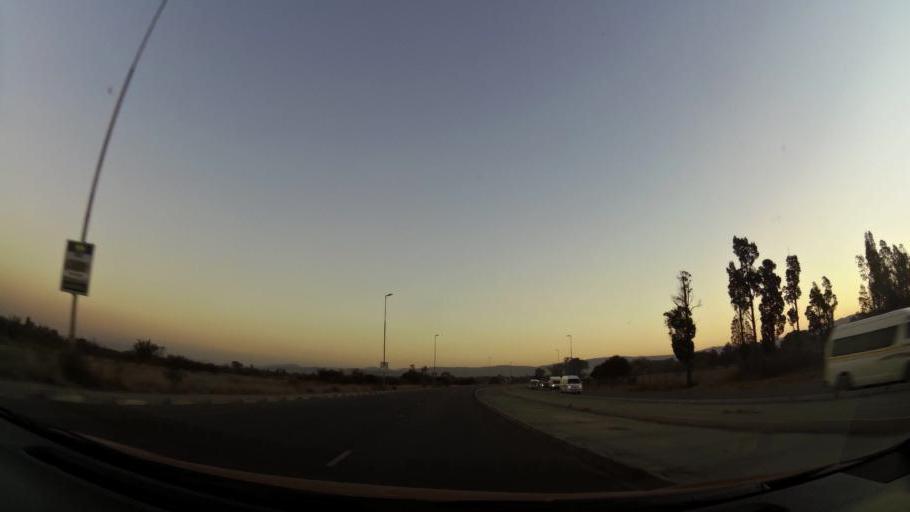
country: ZA
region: North-West
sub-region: Bojanala Platinum District Municipality
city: Rustenburg
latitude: -25.6419
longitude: 27.2623
